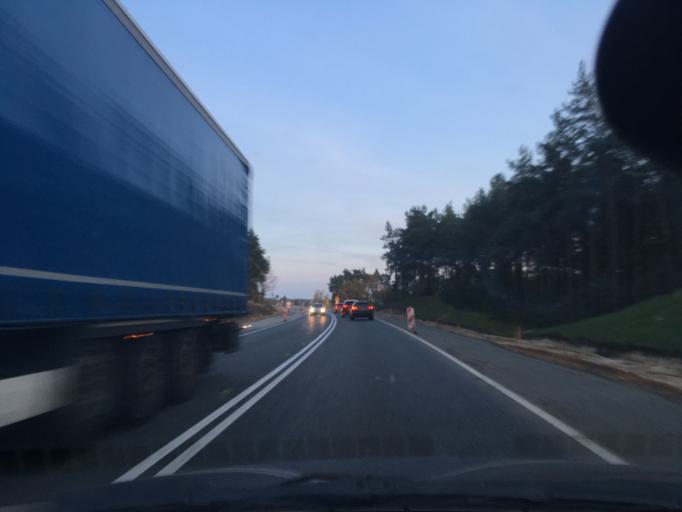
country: PL
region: Masovian Voivodeship
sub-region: Powiat plocki
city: Wyszogrod
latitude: 52.3627
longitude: 20.1964
